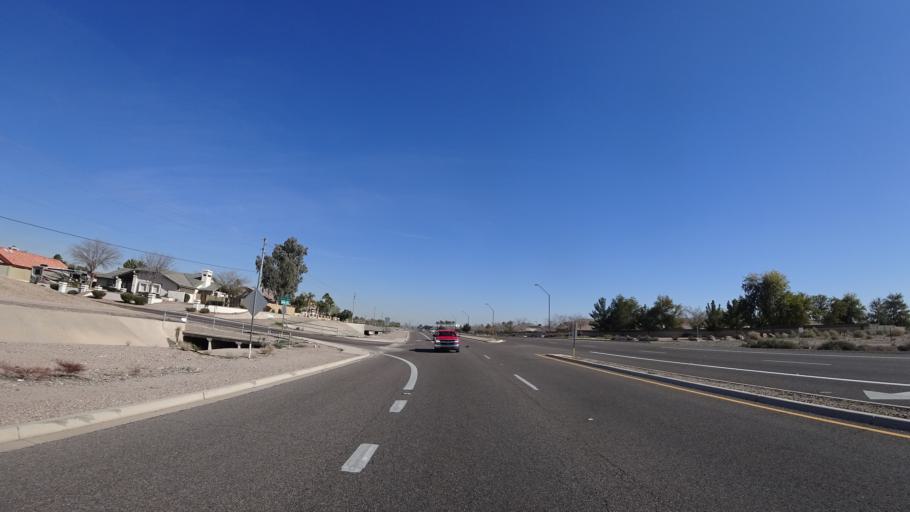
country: US
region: Arizona
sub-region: Maricopa County
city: Litchfield Park
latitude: 33.5077
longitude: -112.3377
